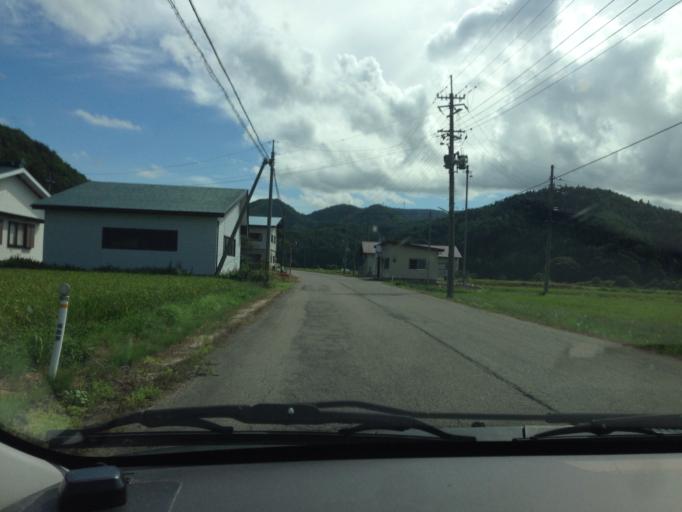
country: JP
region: Fukushima
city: Inawashiro
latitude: 37.3737
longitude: 140.0836
